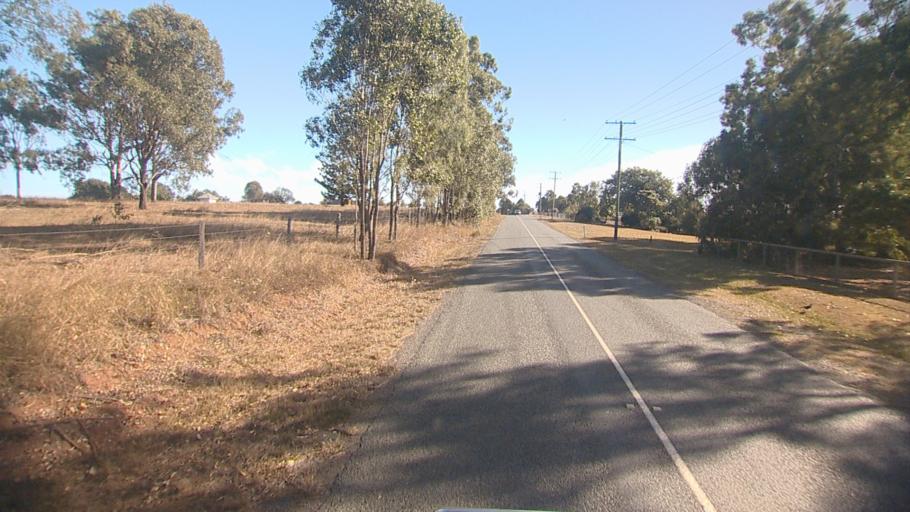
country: AU
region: Queensland
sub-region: Logan
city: Cedar Vale
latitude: -27.8581
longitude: 152.9743
